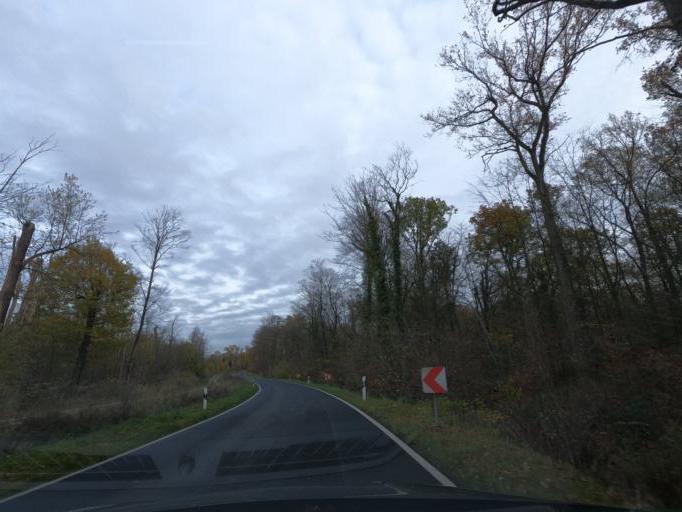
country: DE
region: Lower Saxony
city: Braunschweig
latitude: 52.3173
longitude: 10.5760
